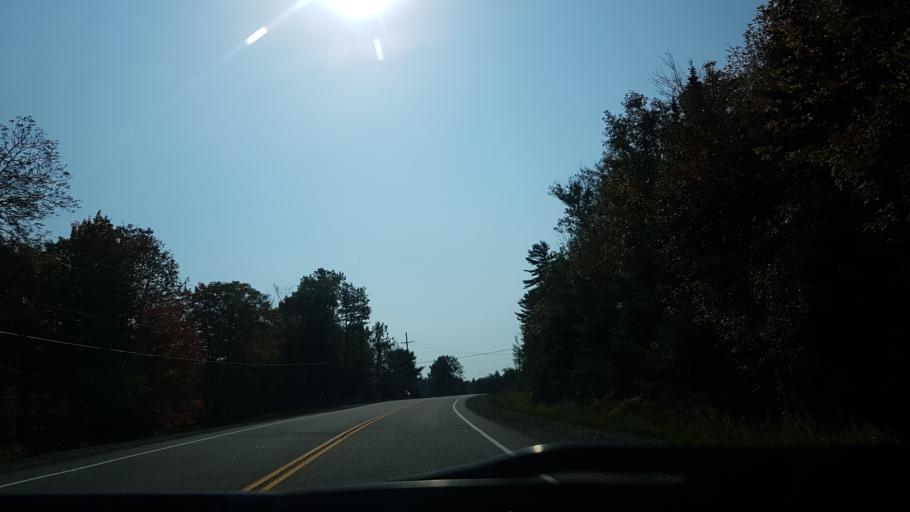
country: CA
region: Ontario
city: Bracebridge
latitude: 44.9883
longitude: -79.2771
